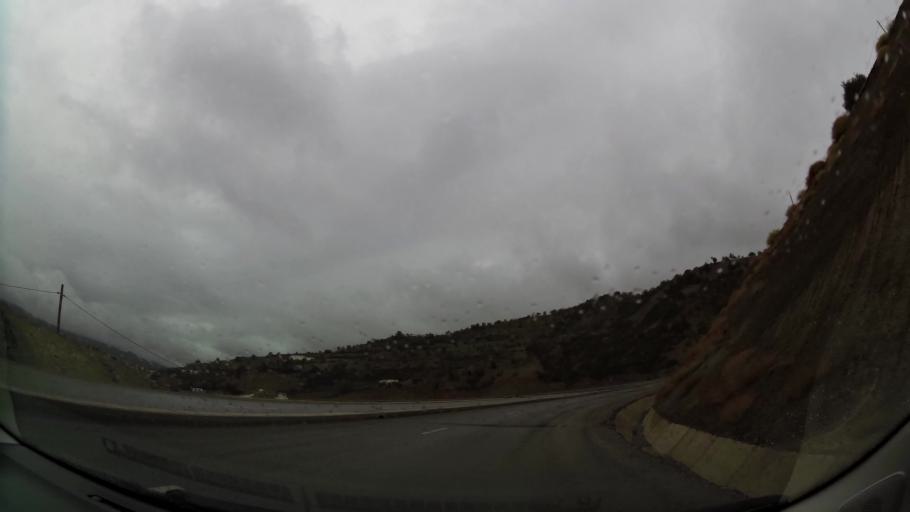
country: MA
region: Taza-Al Hoceima-Taounate
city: Imzourene
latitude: 34.9990
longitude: -3.8124
